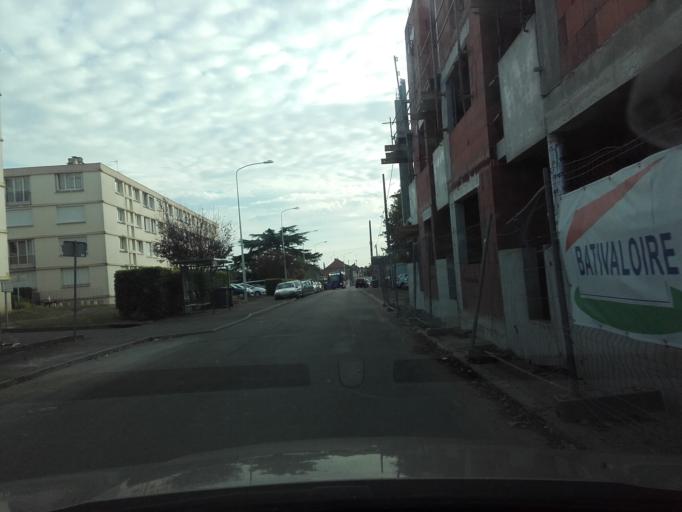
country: FR
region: Centre
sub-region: Departement d'Indre-et-Loire
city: Saint-Cyr-sur-Loire
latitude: 47.4137
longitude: 0.6966
